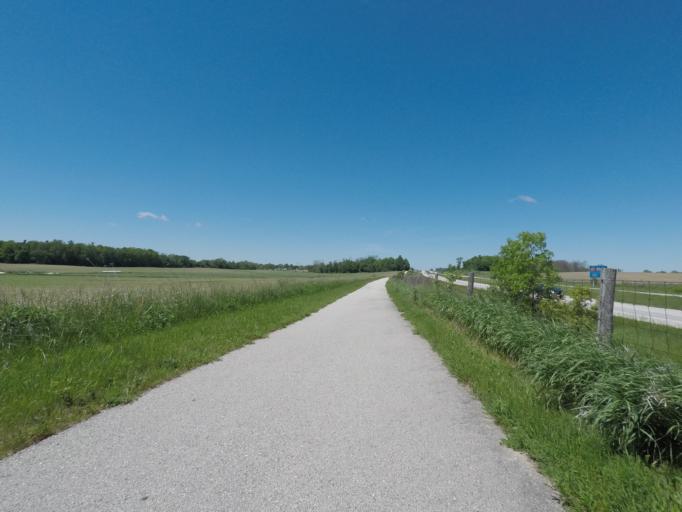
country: US
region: Wisconsin
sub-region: Sheboygan County
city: Kohler
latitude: 43.7503
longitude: -87.8015
